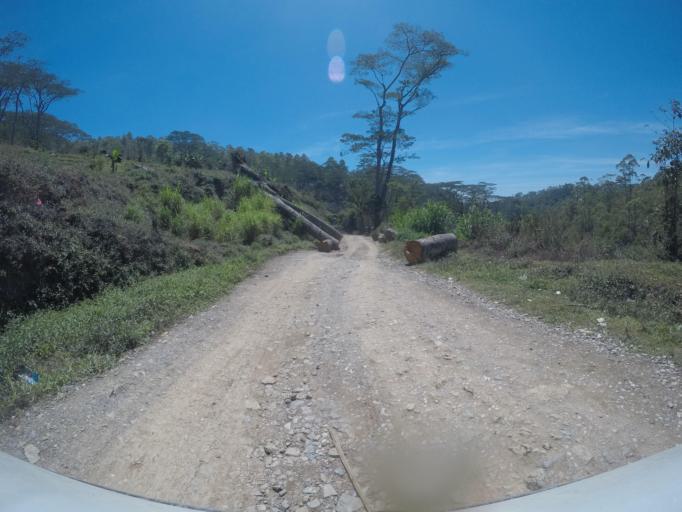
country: TL
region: Ermera
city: Gleno
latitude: -8.7739
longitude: 125.3980
